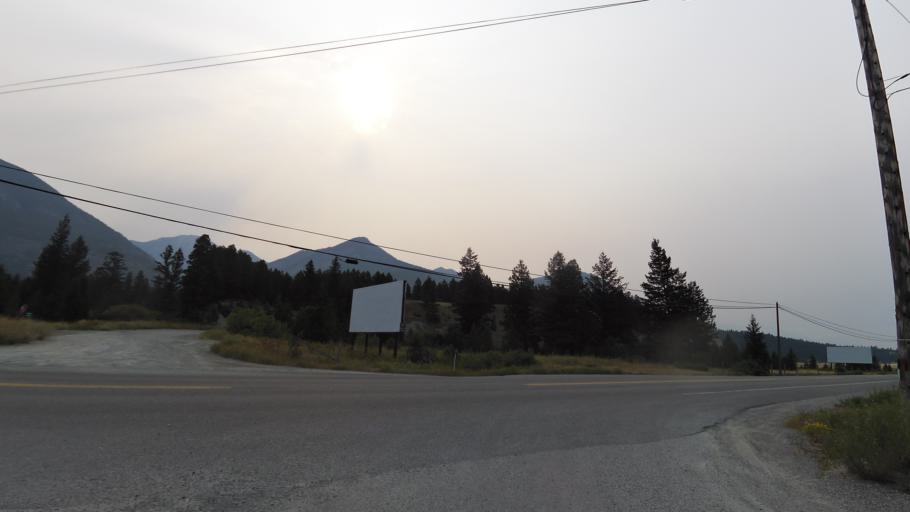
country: CA
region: British Columbia
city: Invermere
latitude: 50.5345
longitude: -116.0067
